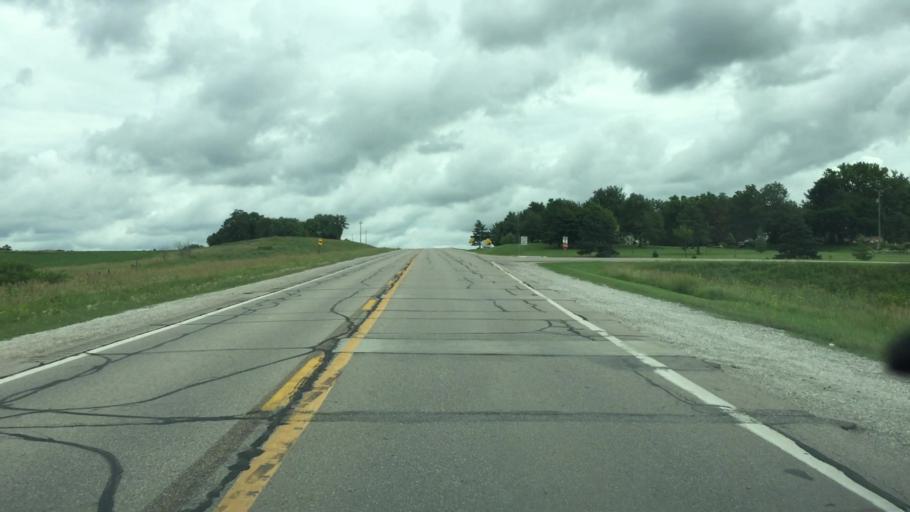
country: US
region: Iowa
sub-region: Jasper County
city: Monroe
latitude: 41.5428
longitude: -93.0986
